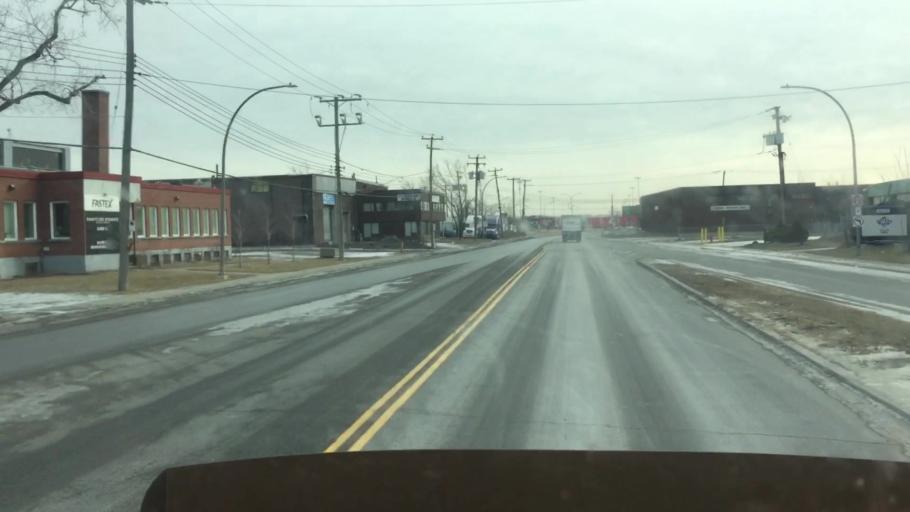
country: CA
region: Quebec
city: Dorval
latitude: 45.4635
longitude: -73.7175
